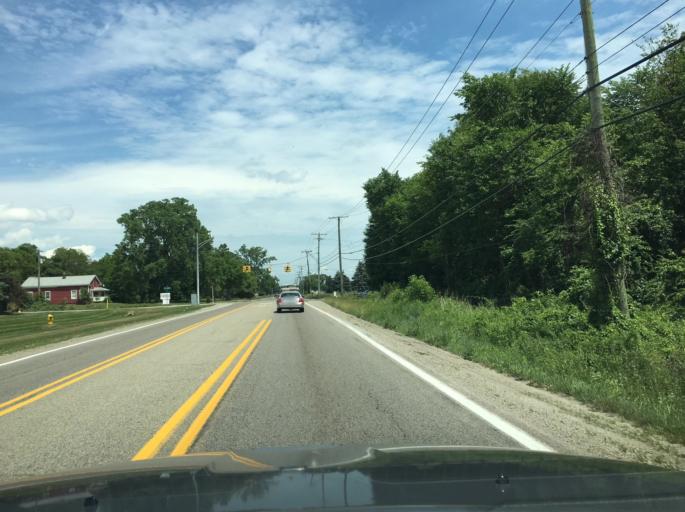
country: US
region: Michigan
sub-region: Macomb County
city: Shelby
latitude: 42.7147
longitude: -82.9977
